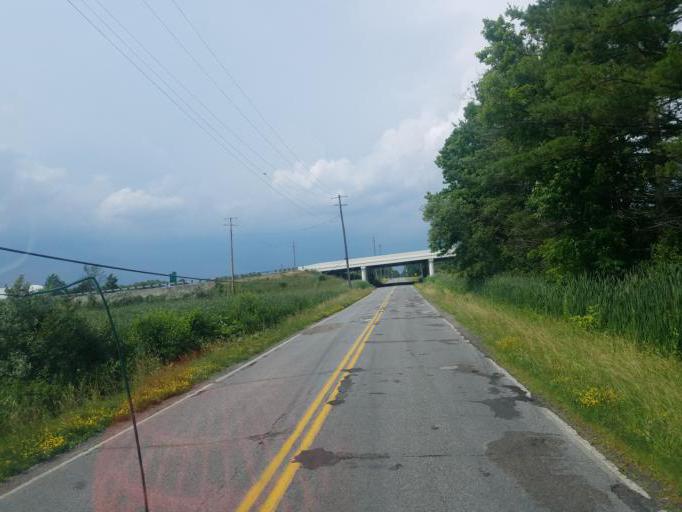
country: US
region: Ohio
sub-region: Portage County
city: Ravenna
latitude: 41.1060
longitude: -81.2203
